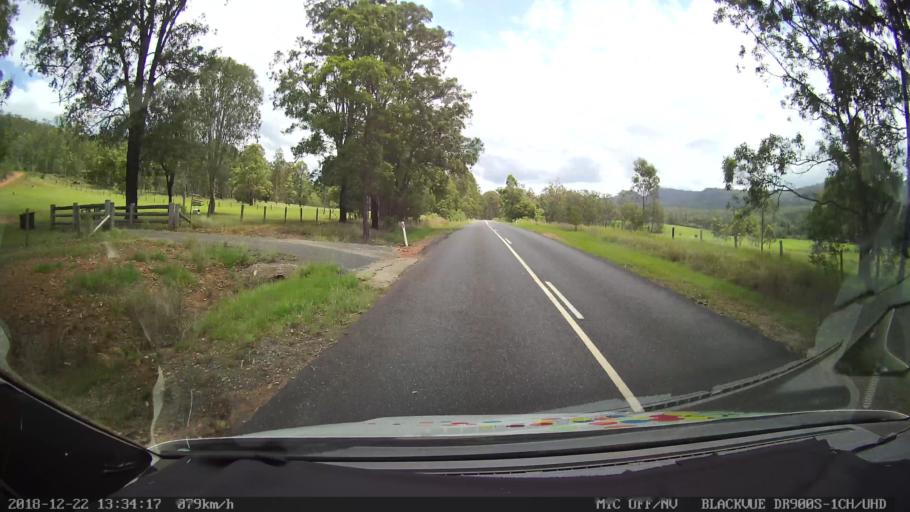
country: AU
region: New South Wales
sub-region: Clarence Valley
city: Coutts Crossing
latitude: -29.8690
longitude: 152.8189
